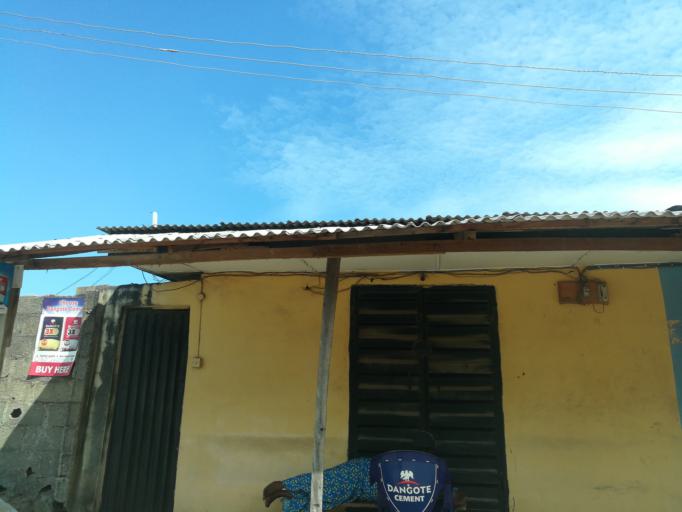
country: NG
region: Lagos
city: Ebute Ikorodu
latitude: 6.6001
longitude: 3.5016
